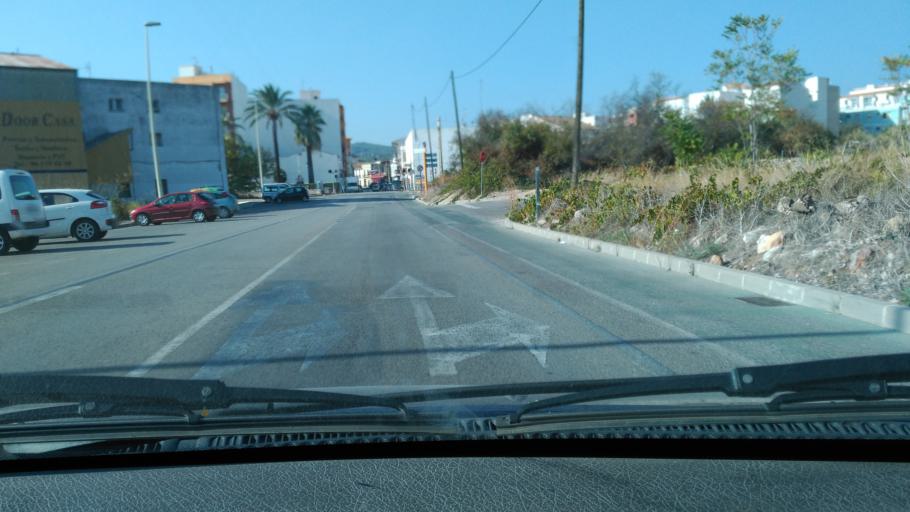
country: ES
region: Valencia
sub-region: Provincia de Alicante
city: Gata de Gorgos
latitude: 38.7786
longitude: 0.0859
